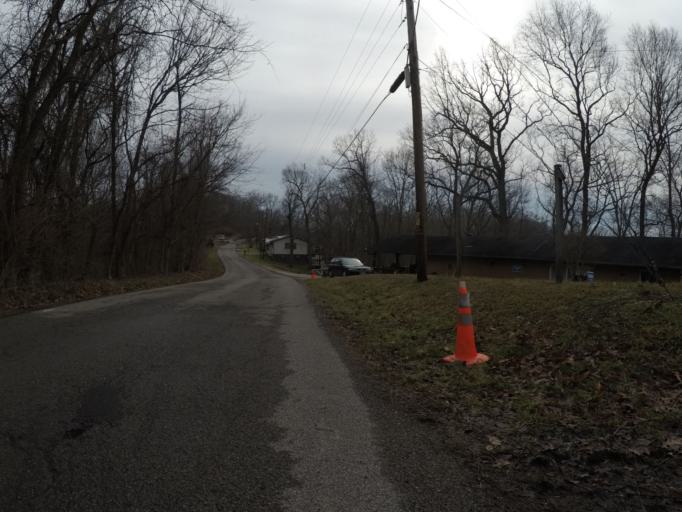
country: US
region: West Virginia
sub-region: Wayne County
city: Lavalette
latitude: 38.3652
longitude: -82.4145
